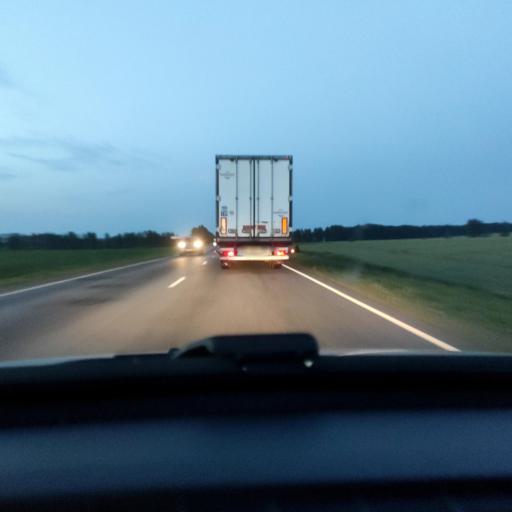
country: RU
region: Voronezj
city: Verkhnyaya Khava
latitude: 51.6804
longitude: 39.8951
